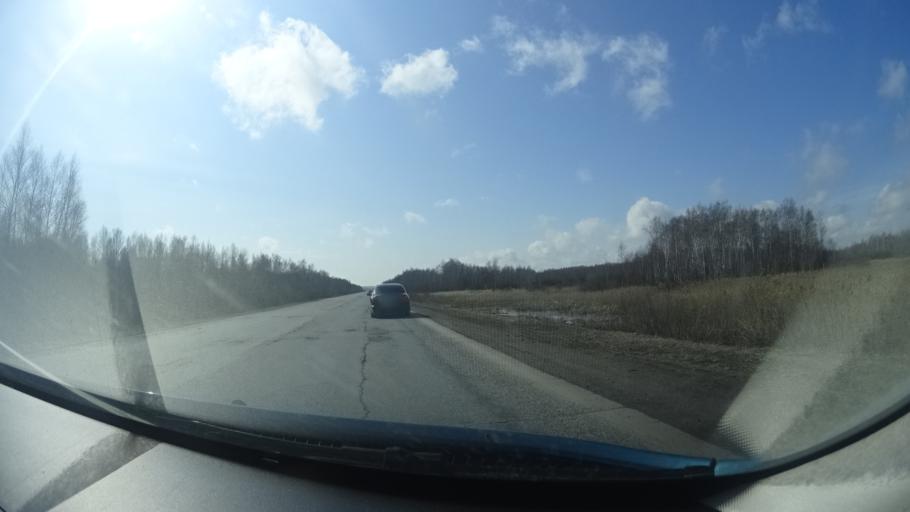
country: RU
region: Bashkortostan
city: Mikhaylovka
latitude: 54.9112
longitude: 55.7326
